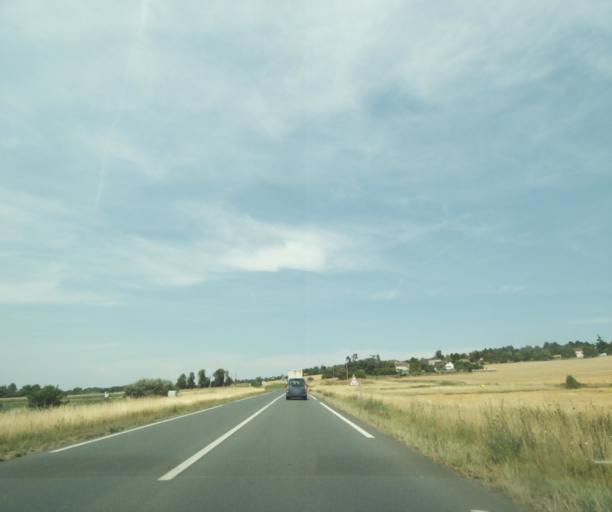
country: FR
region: Poitou-Charentes
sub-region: Departement de la Vienne
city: Chatellerault
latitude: 46.8061
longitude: 0.5653
